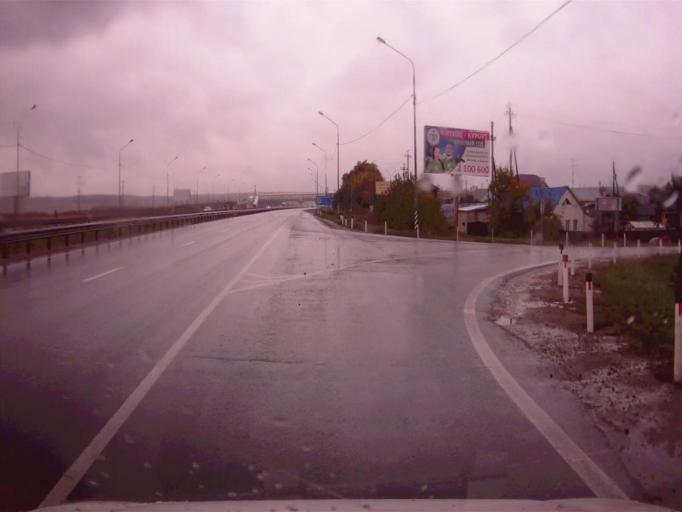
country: RU
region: Chelyabinsk
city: Dolgoderevenskoye
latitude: 55.3081
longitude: 61.3355
